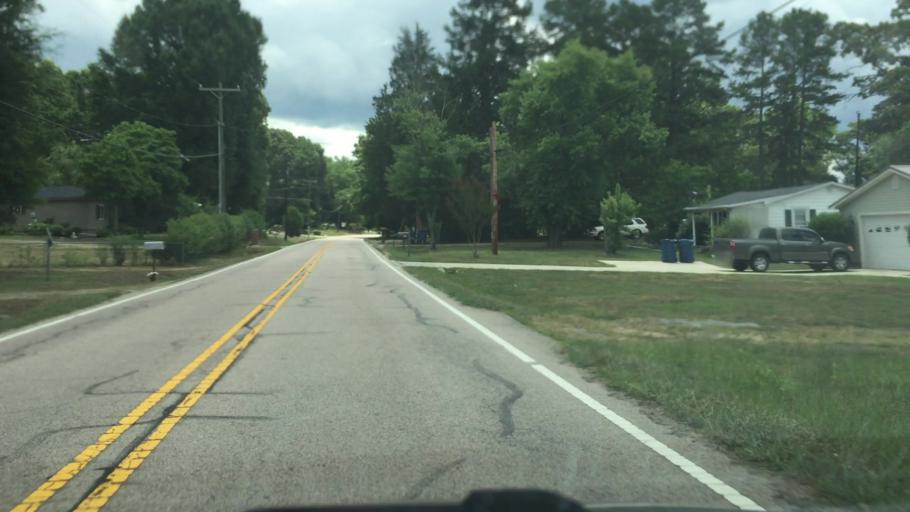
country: US
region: North Carolina
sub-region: Rowan County
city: Enochville
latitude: 35.5017
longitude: -80.6683
